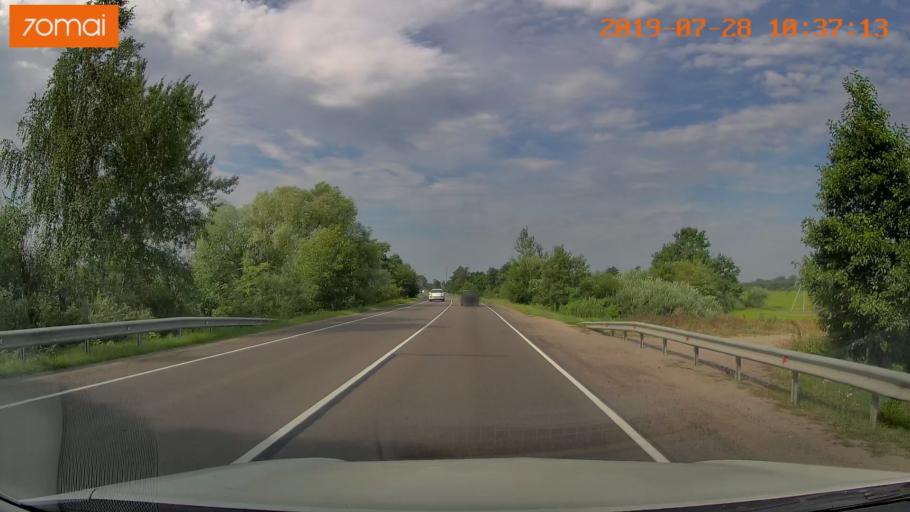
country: RU
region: Kaliningrad
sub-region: Gorod Kaliningrad
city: Kaliningrad
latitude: 54.7327
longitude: 20.4118
